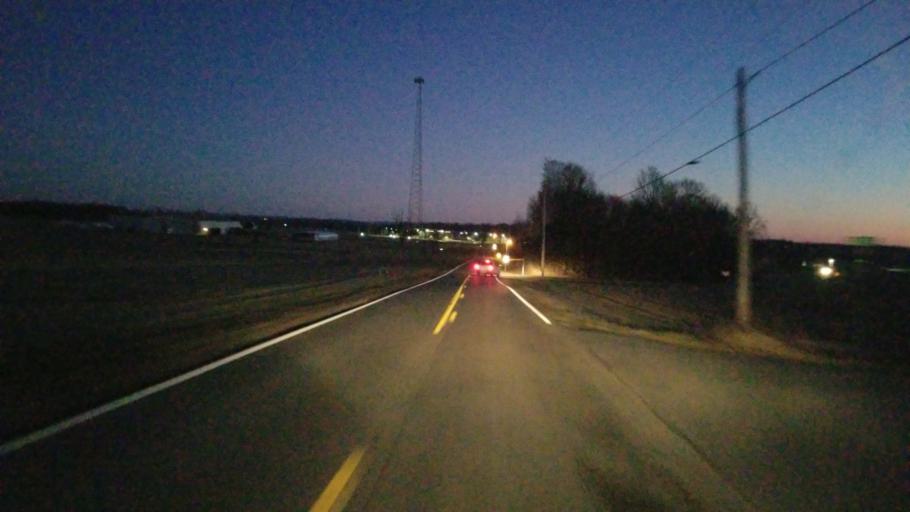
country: US
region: Ohio
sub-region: Highland County
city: Leesburg
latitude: 39.3354
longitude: -83.5499
